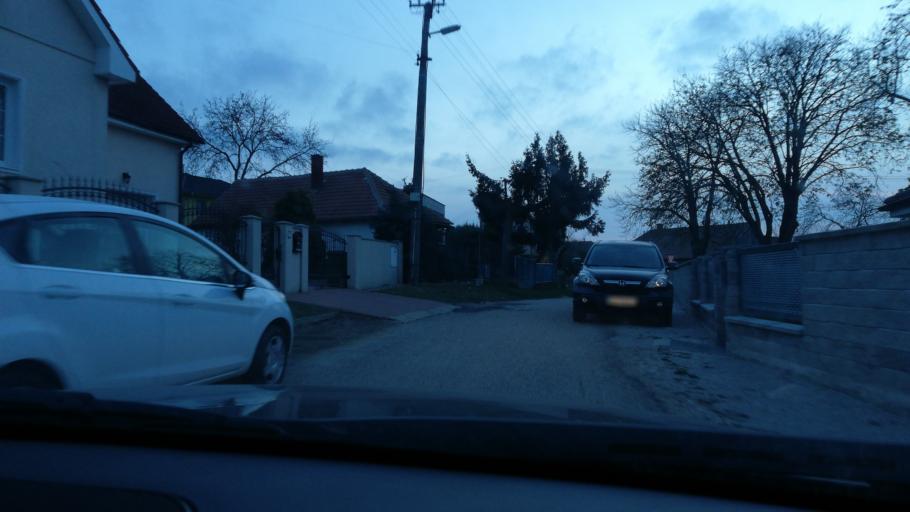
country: SK
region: Nitriansky
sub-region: Okres Nitra
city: Nitra
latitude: 48.3102
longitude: 17.9933
